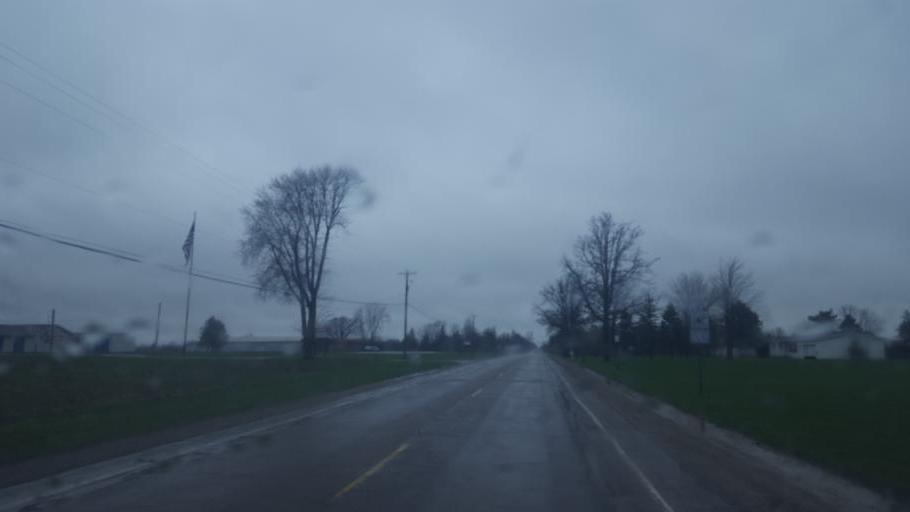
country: US
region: Michigan
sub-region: Isabella County
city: Mount Pleasant
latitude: 43.6548
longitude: -84.7681
